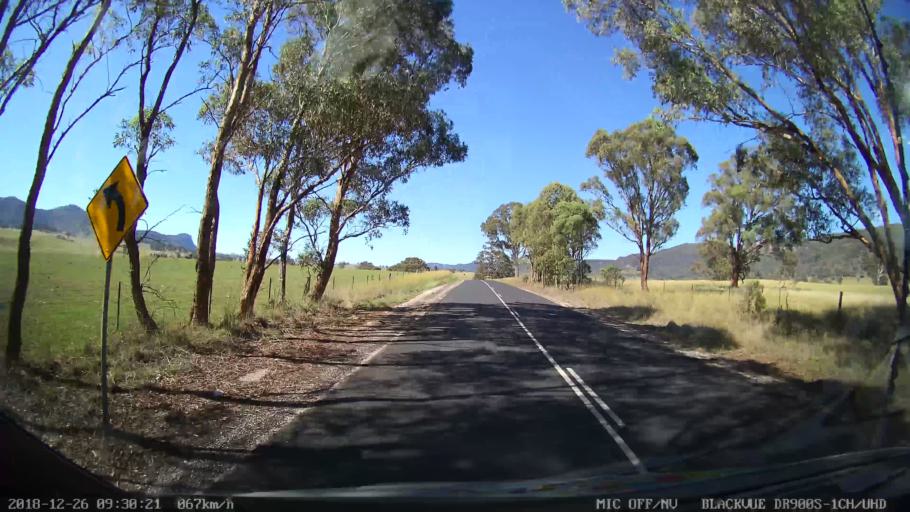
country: AU
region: New South Wales
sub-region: Mid-Western Regional
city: Kandos
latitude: -32.8620
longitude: 150.0294
